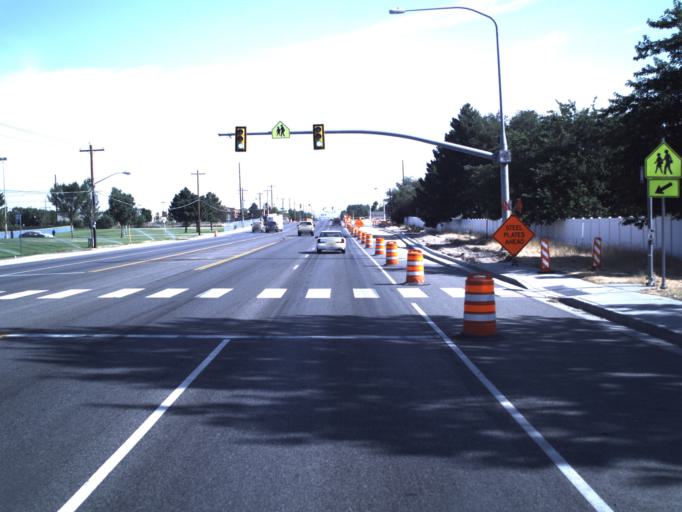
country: US
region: Utah
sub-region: Salt Lake County
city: West Valley City
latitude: 40.6787
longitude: -112.0247
